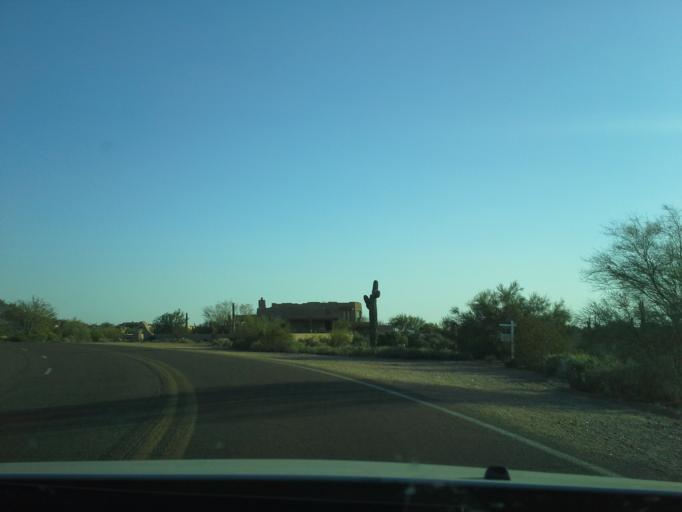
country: US
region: Arizona
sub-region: Pinal County
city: Apache Junction
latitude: 33.3756
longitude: -111.4336
